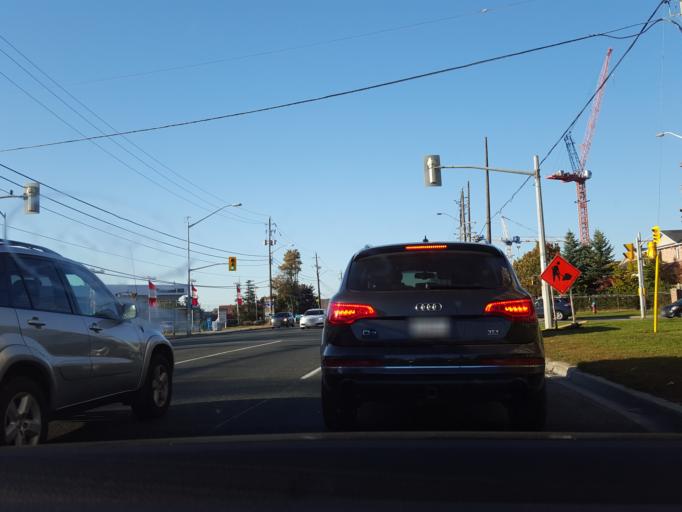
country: CA
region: Ontario
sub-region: York
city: Richmond Hill
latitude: 43.8496
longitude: -79.4321
